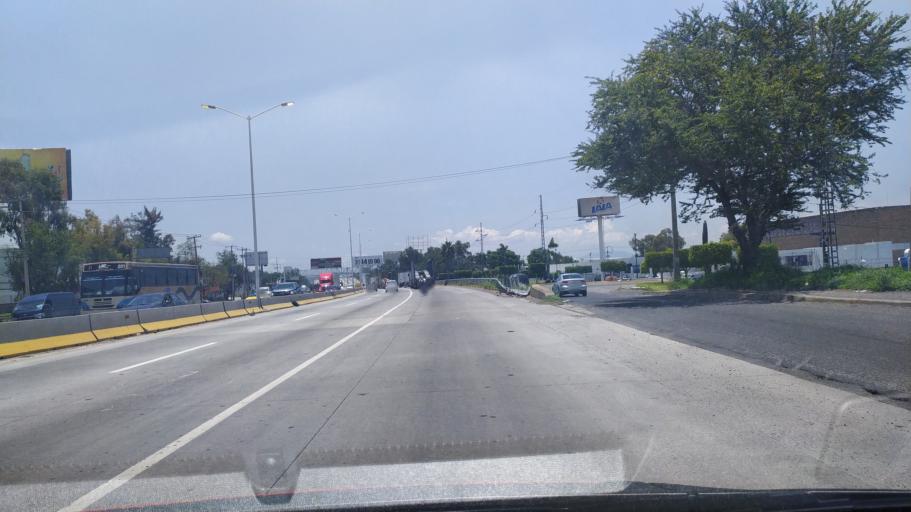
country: MX
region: Jalisco
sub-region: Tlajomulco de Zuniga
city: Altus Bosques
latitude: 20.5766
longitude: -103.3594
